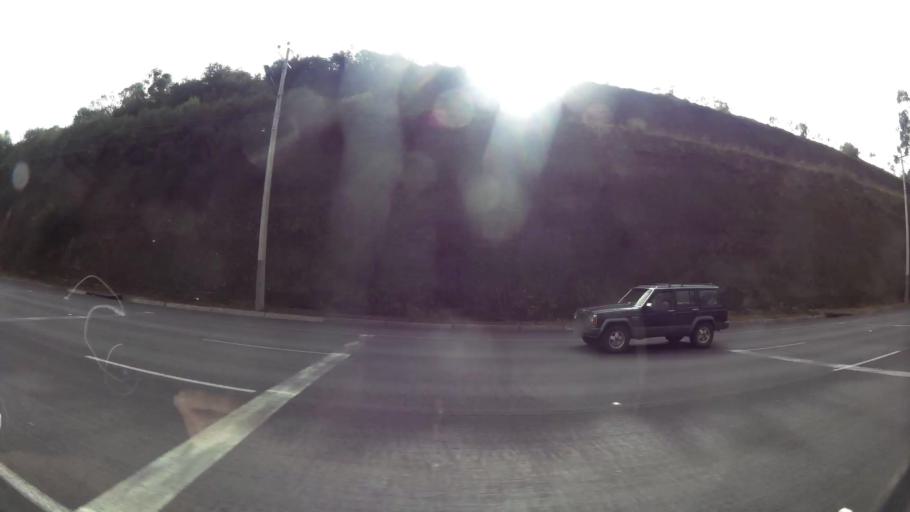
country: EC
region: Pichincha
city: Sangolqui
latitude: -0.3942
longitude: -78.5362
